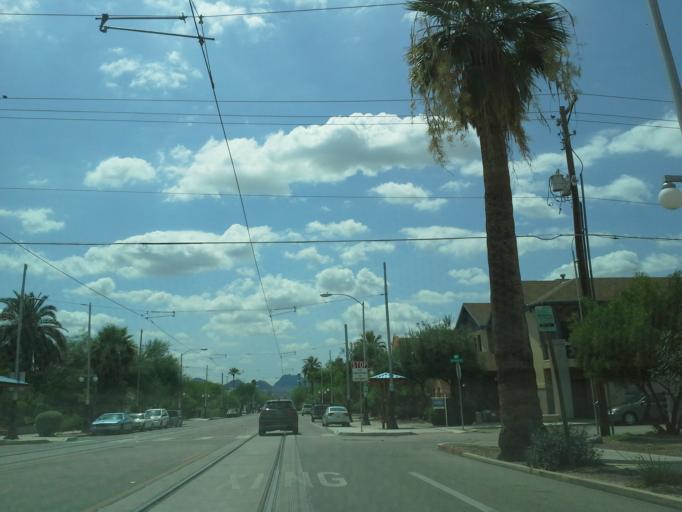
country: US
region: Arizona
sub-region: Pima County
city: South Tucson
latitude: 32.2317
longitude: -110.9615
